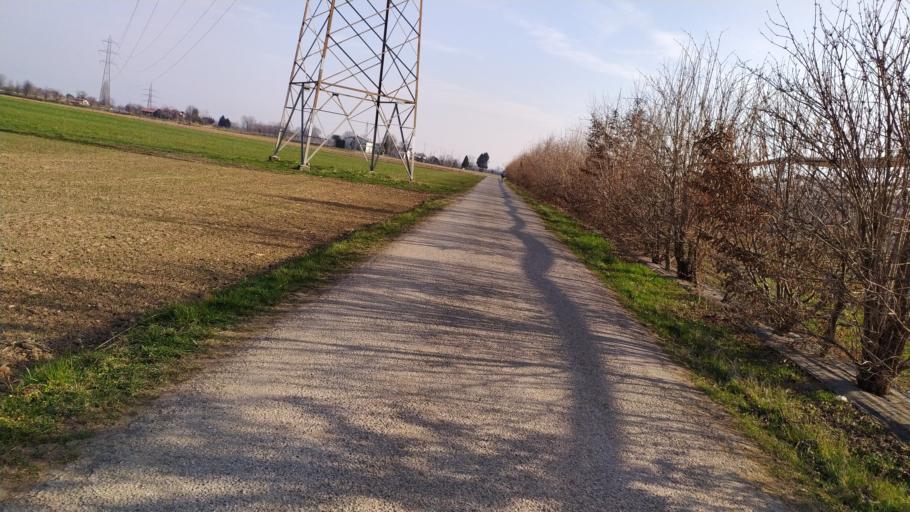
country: IT
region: Veneto
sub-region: Provincia di Vicenza
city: Giavenale
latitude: 45.6950
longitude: 11.3994
